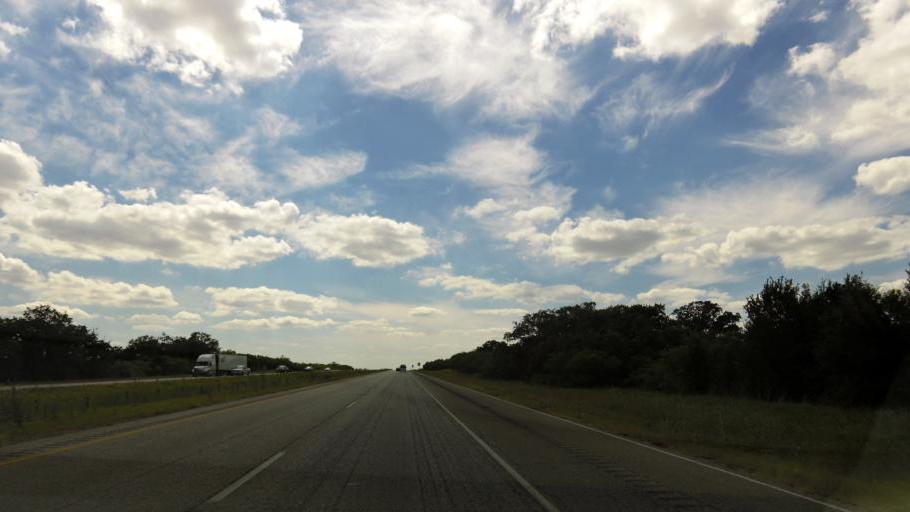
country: US
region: Texas
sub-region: Gonzales County
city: Waelder
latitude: 29.6687
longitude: -97.3108
